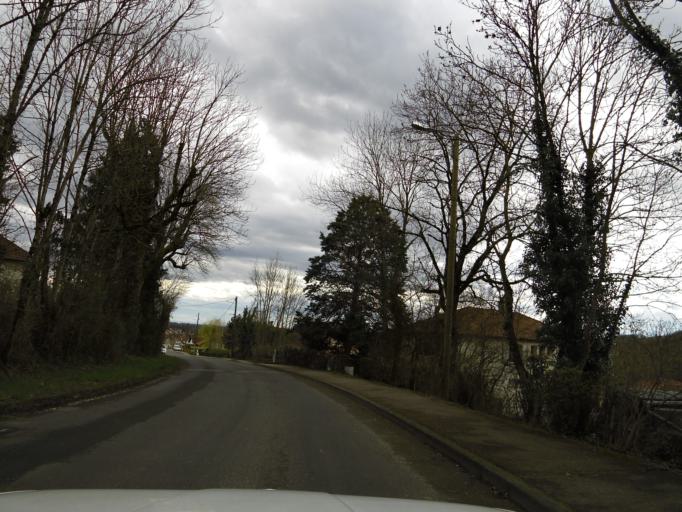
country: FR
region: Rhone-Alpes
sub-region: Departement de l'Ain
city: Meximieux
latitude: 45.9257
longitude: 5.2264
